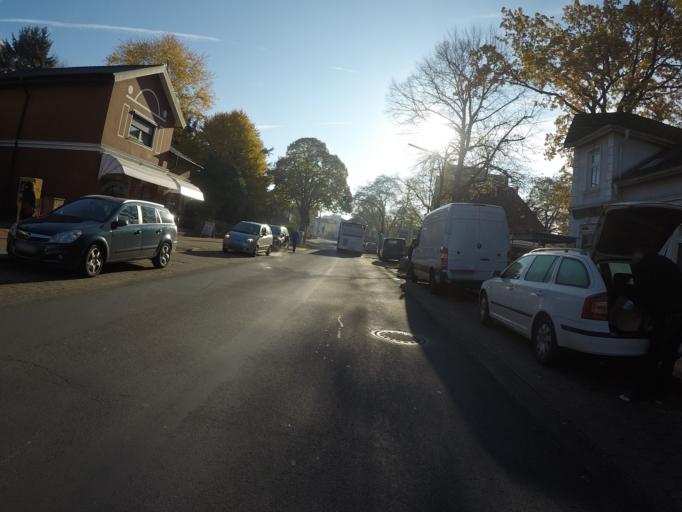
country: DE
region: Hamburg
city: Eidelstedt
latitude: 53.6330
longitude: 9.9205
